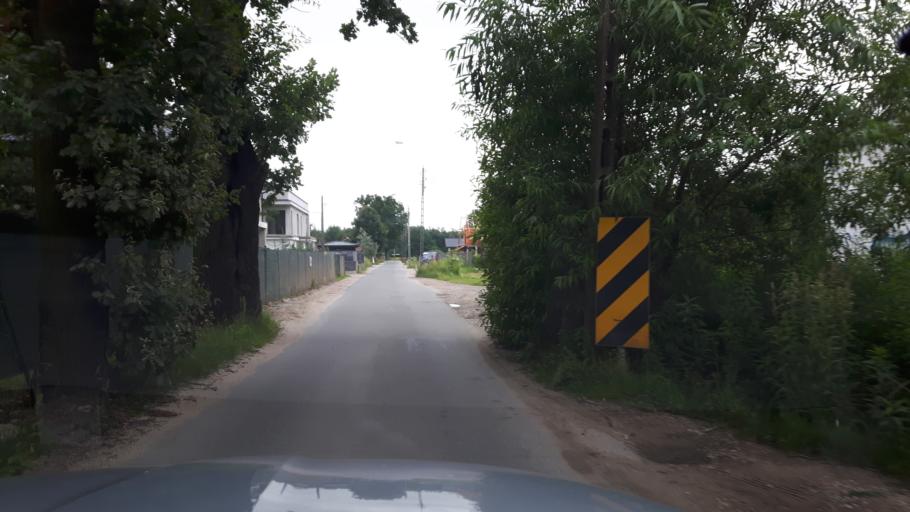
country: PL
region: Masovian Voivodeship
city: Zielonka
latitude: 52.2877
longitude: 21.1693
